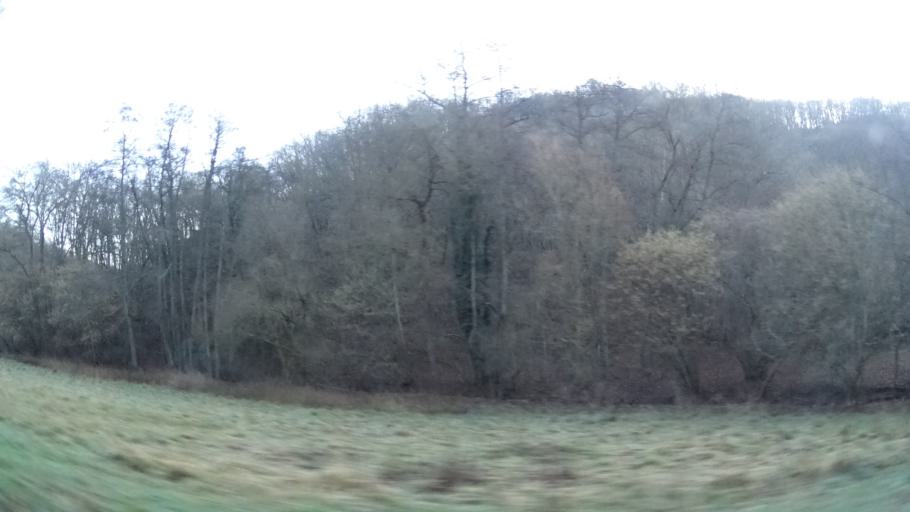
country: DE
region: Rheinland-Pfalz
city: Nieder-Wiesen
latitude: 49.7487
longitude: 7.9770
